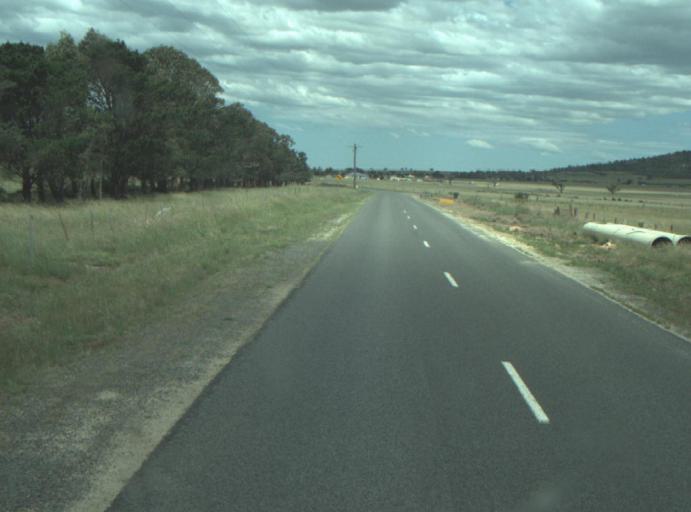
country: AU
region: Victoria
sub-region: Wyndham
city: Little River
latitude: -37.9105
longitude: 144.4627
